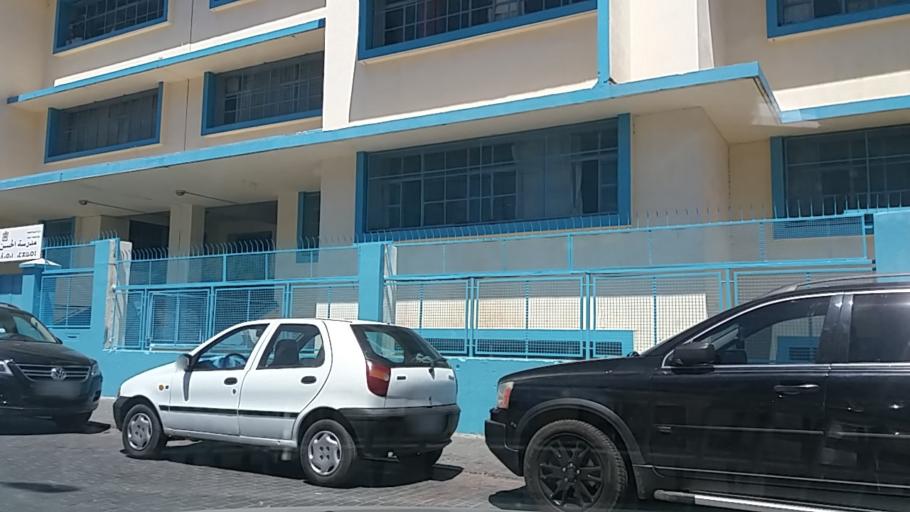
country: MA
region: Tanger-Tetouan
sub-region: Tanger-Assilah
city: Tangier
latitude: 35.7858
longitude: -5.8153
